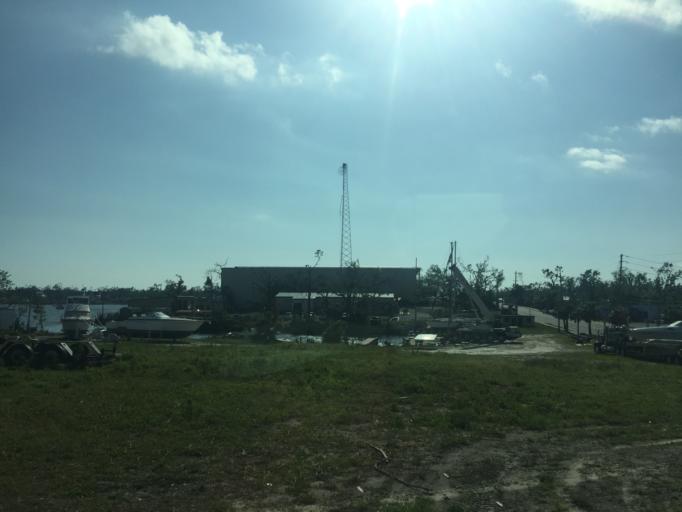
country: US
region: Florida
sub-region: Bay County
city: Cedar Grove
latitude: 30.1563
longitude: -85.6356
